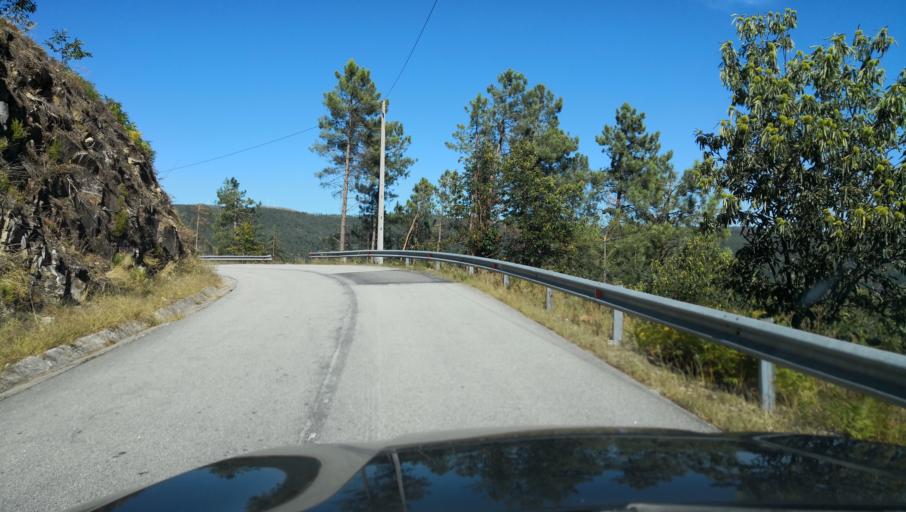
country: PT
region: Vila Real
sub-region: Santa Marta de Penaguiao
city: Santa Marta de Penaguiao
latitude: 41.2540
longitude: -7.8562
